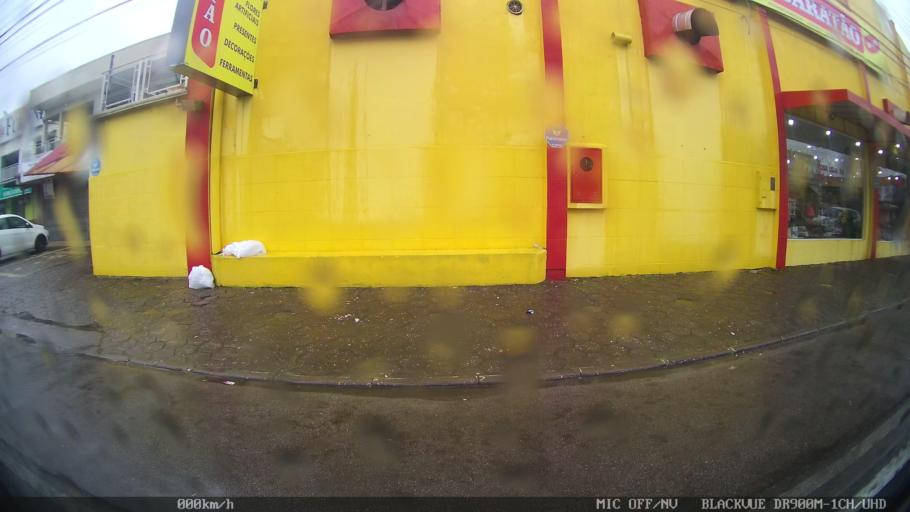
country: BR
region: Santa Catarina
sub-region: Itajai
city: Itajai
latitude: -26.9070
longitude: -48.6776
